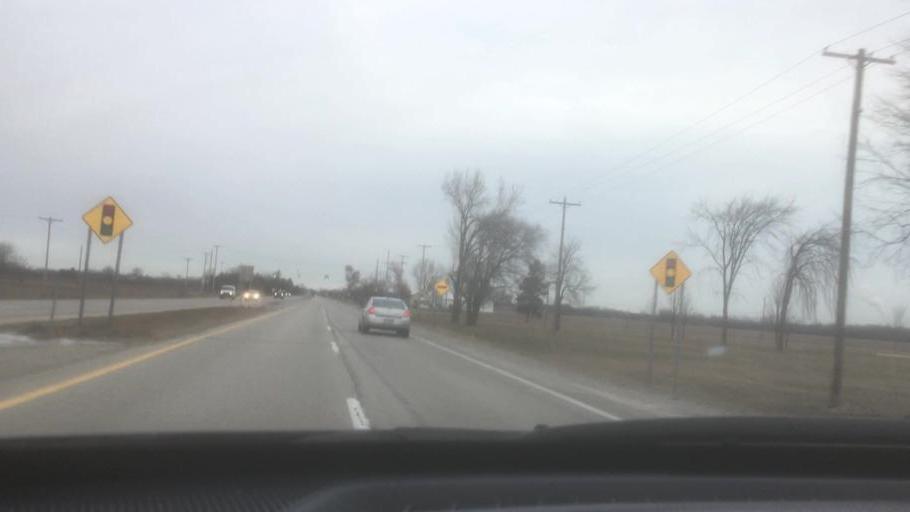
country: US
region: Michigan
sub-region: Bay County
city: Essexville
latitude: 43.5638
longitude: -83.8429
